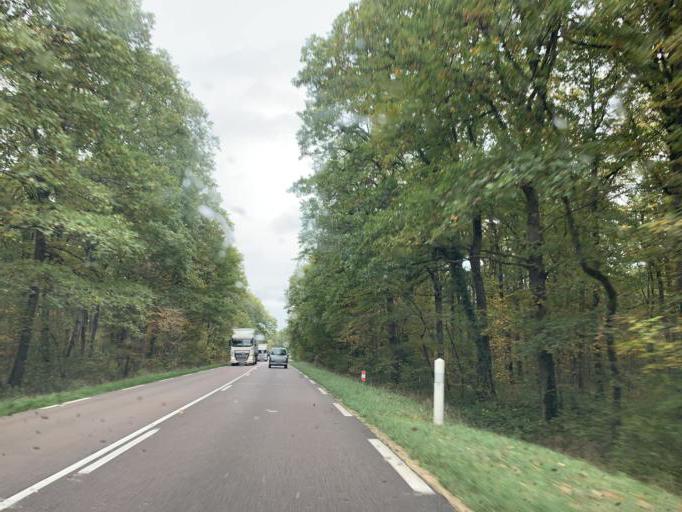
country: FR
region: Bourgogne
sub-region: Departement de l'Yonne
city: Moneteau
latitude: 47.8443
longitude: 3.6201
